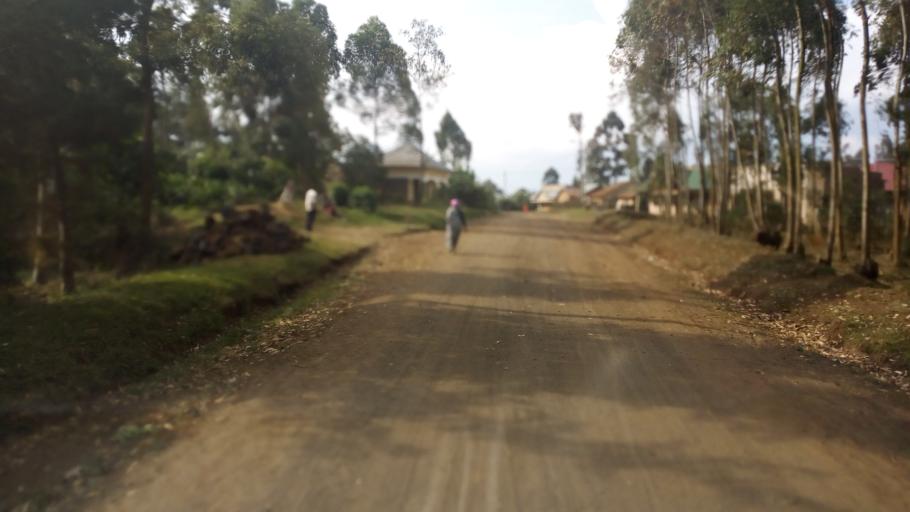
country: UG
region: Western Region
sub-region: Kisoro District
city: Kisoro
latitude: -1.2963
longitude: 29.7007
